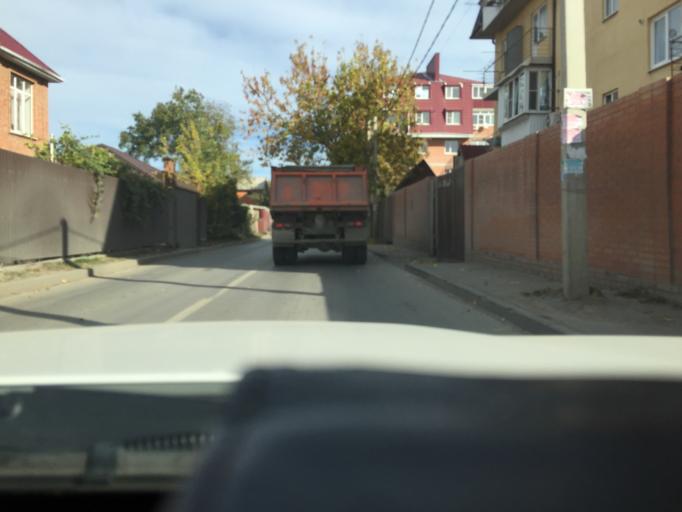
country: RU
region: Rostov
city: Imeni Chkalova
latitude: 47.2806
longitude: 39.7995
